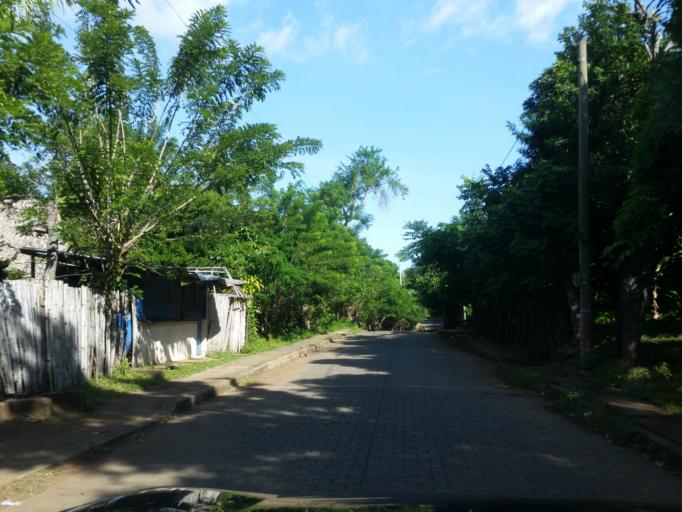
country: NI
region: Masaya
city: Catarina
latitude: 11.9343
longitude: -86.0686
